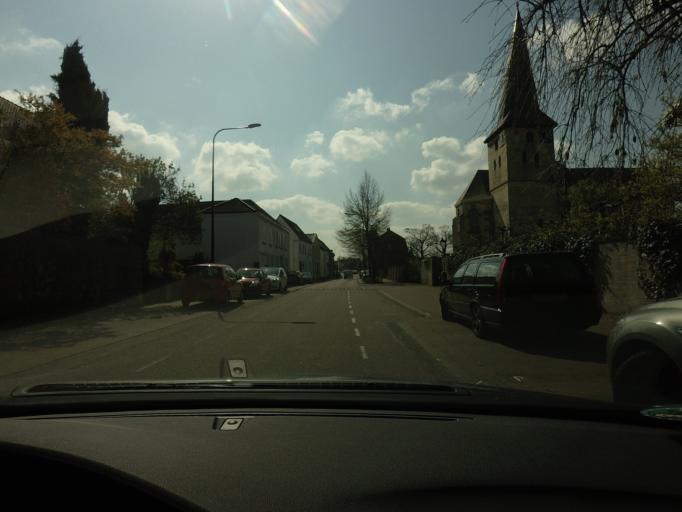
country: NL
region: Limburg
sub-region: Gemeente Maastricht
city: Heer
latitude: 50.8128
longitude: 5.7302
